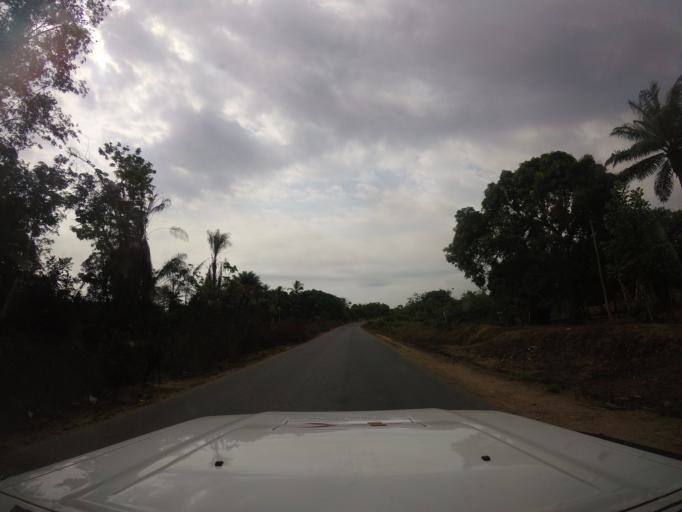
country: LR
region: Montserrado
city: Monrovia
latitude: 6.5619
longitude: -10.8715
